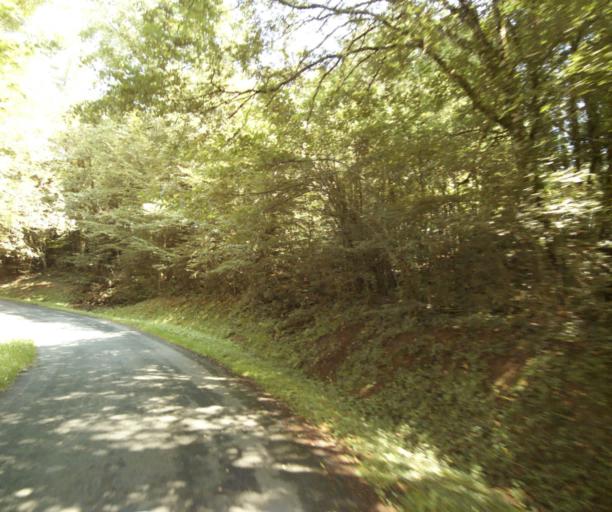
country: FR
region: Limousin
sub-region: Departement de la Correze
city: Sainte-Fortunade
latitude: 45.2045
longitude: 1.8362
